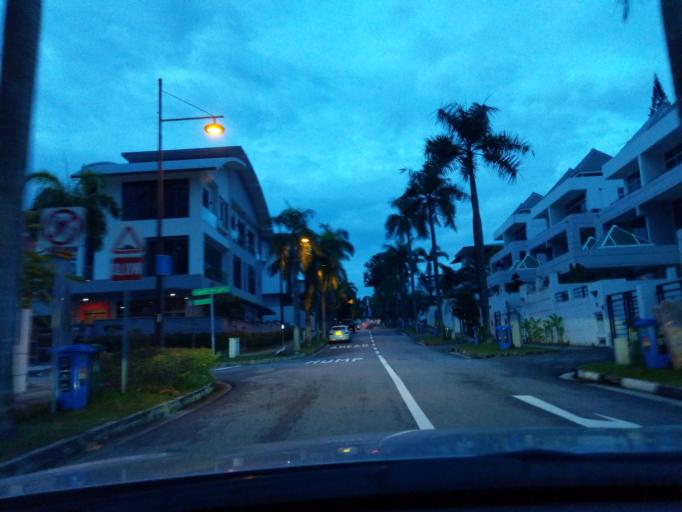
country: SG
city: Singapore
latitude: 1.3154
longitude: 103.9402
